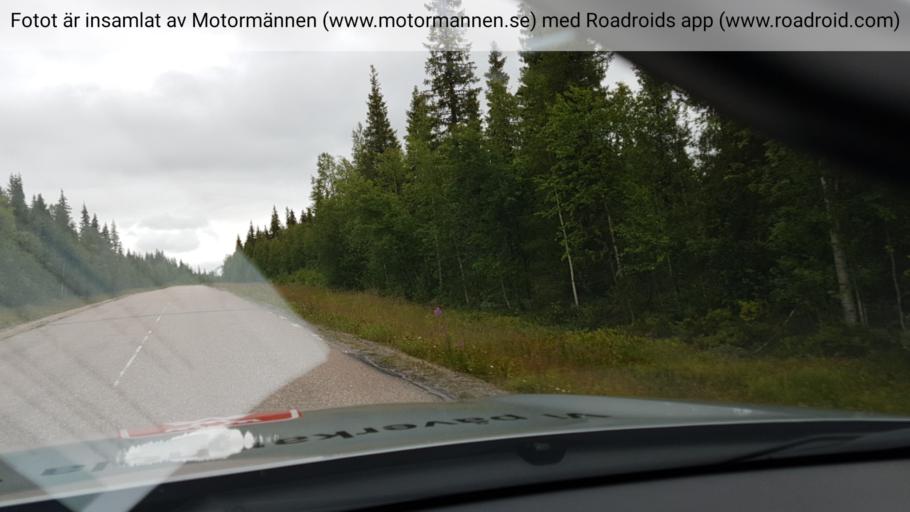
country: SE
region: Norrbotten
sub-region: Overkalix Kommun
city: OEverkalix
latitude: 67.0403
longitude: 22.0390
